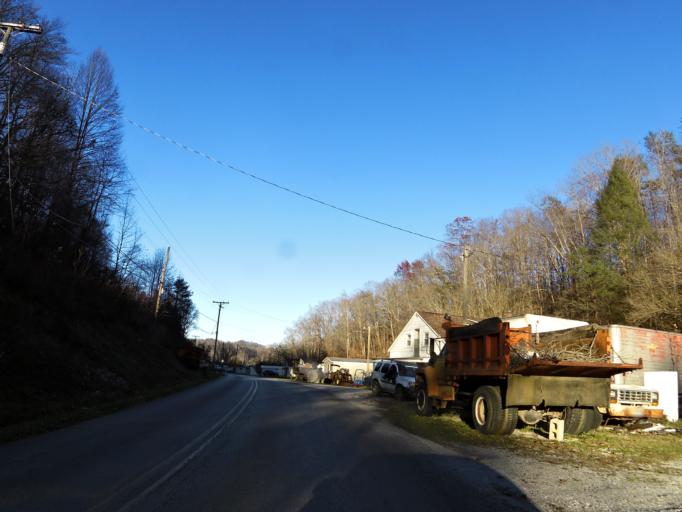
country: US
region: Tennessee
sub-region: Anderson County
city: Rocky Top
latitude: 36.2018
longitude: -84.1500
